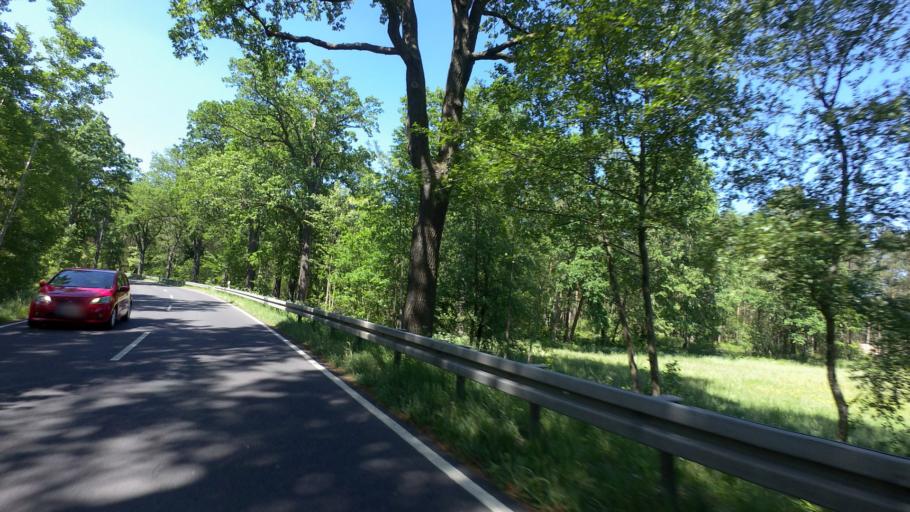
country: DE
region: Brandenburg
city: Schlepzig
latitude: 52.0650
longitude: 13.9168
